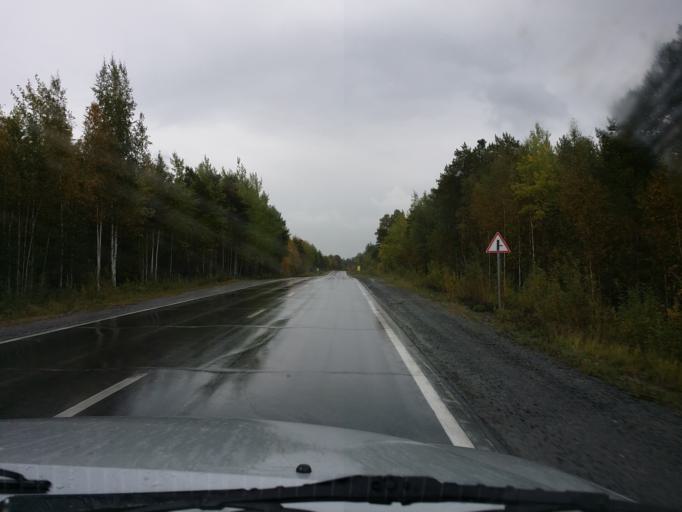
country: RU
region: Khanty-Mansiyskiy Avtonomnyy Okrug
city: Megion
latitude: 61.1625
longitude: 75.6782
